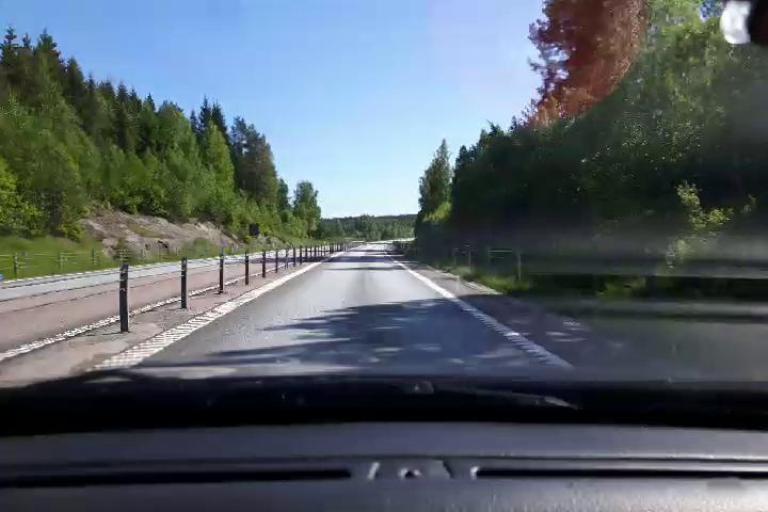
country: SE
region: Gaevleborg
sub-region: Soderhamns Kommun
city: Soderhamn
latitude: 61.2828
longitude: 17.0265
